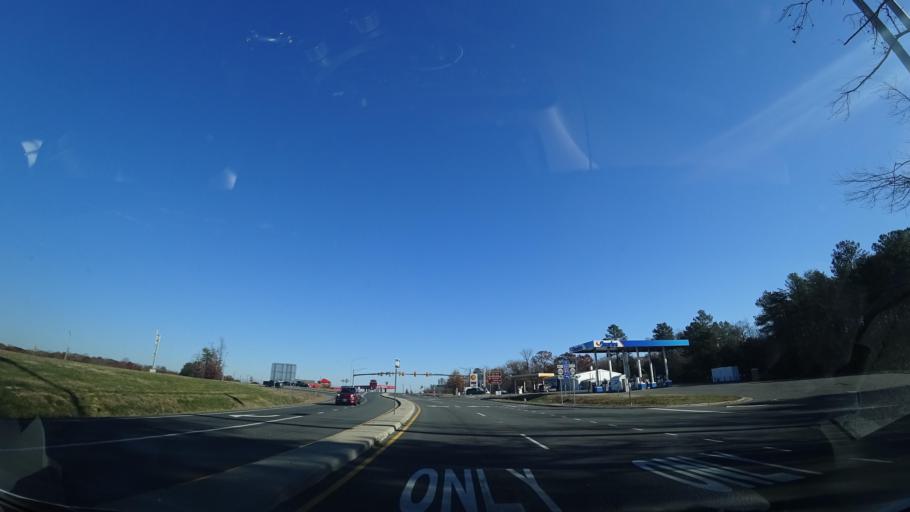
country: US
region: Virginia
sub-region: Spotsylvania County
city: Spotsylvania Courthouse
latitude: 38.1311
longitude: -77.5102
